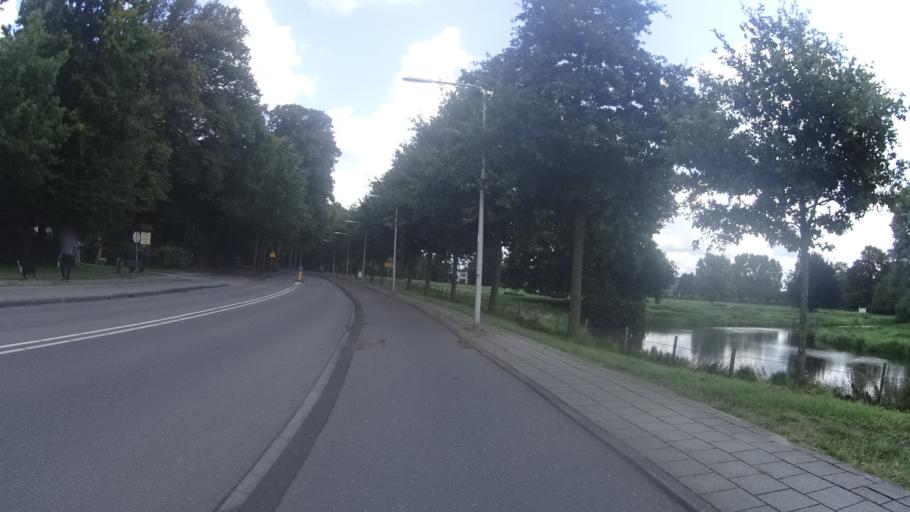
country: NL
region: North Holland
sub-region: Gemeente Bloemendaal
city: Bloemendaal
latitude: 52.4072
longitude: 4.6252
